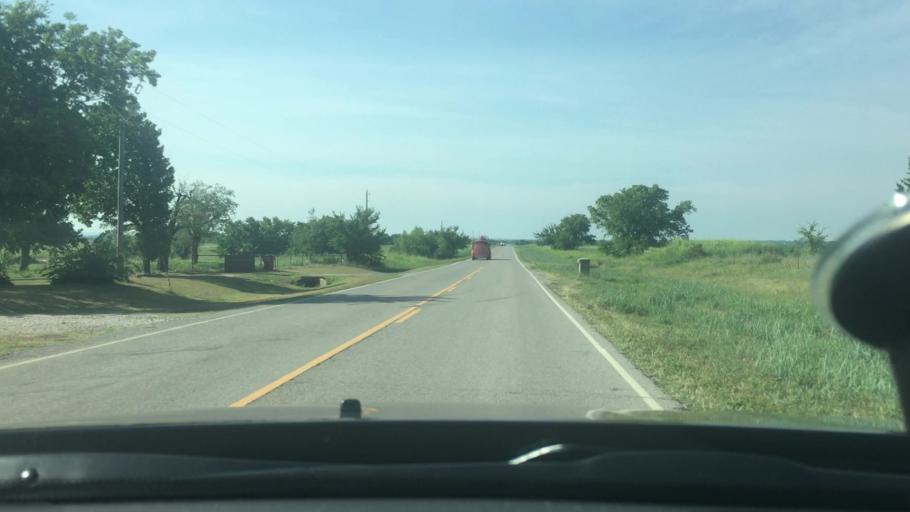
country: US
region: Oklahoma
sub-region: Garvin County
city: Maysville
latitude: 34.6675
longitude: -97.4054
